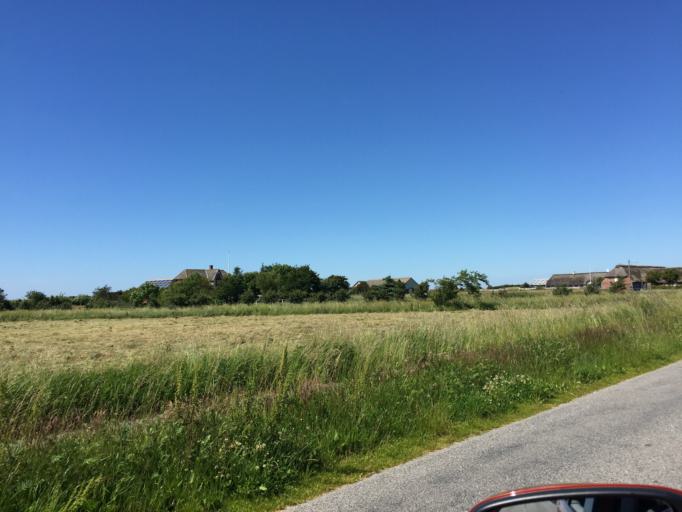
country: DE
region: Schleswig-Holstein
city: List
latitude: 55.1729
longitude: 8.5563
